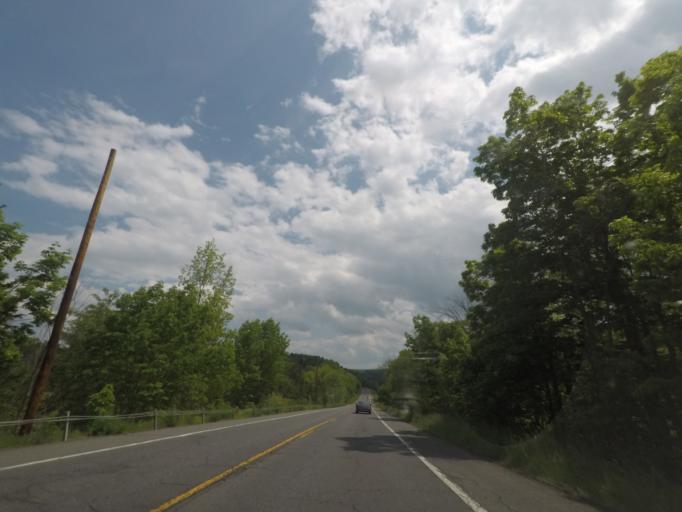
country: US
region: New York
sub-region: Columbia County
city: Oakdale
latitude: 42.1327
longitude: -73.7297
